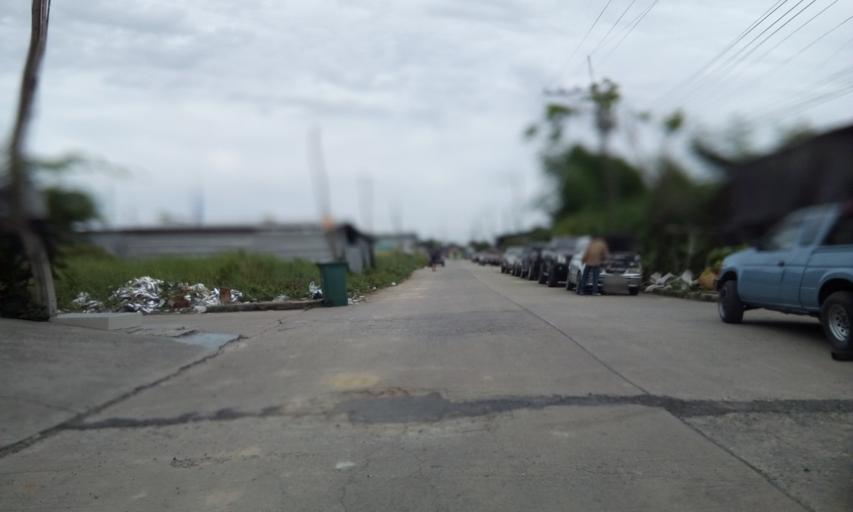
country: TH
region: Pathum Thani
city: Nong Suea
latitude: 14.0689
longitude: 100.8786
